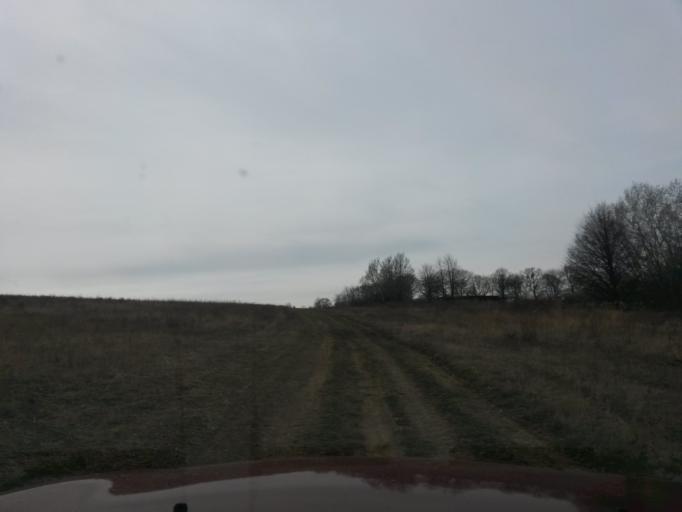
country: HU
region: Borsod-Abauj-Zemplen
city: Gonc
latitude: 48.5850
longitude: 21.3774
